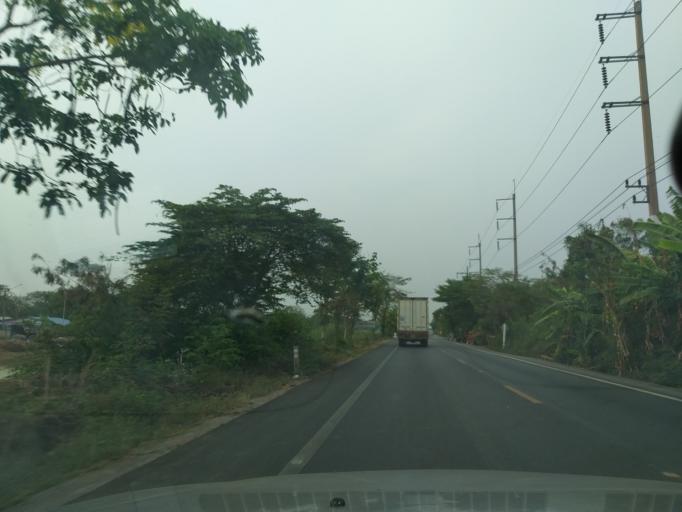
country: TH
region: Pathum Thani
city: Ban Lam Luk Ka
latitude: 13.9772
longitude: 100.8956
